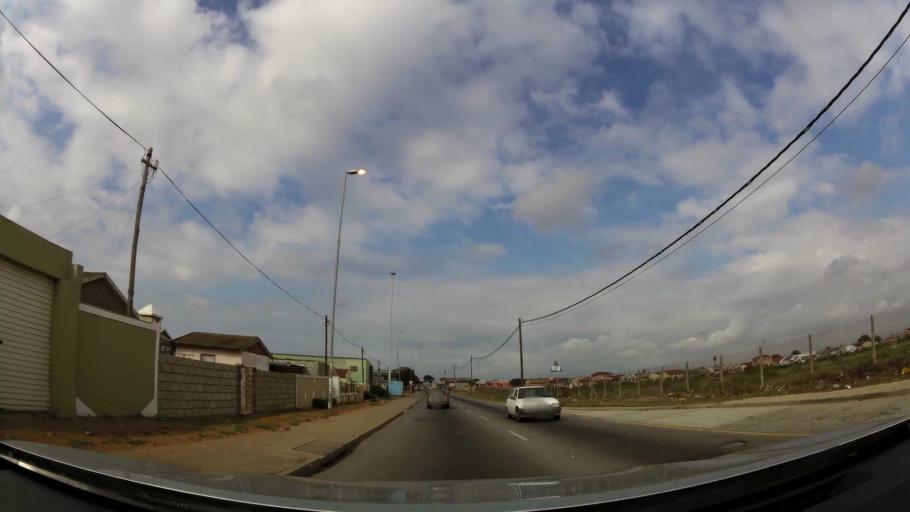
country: ZA
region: Eastern Cape
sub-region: Nelson Mandela Bay Metropolitan Municipality
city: Port Elizabeth
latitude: -33.8177
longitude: 25.5843
